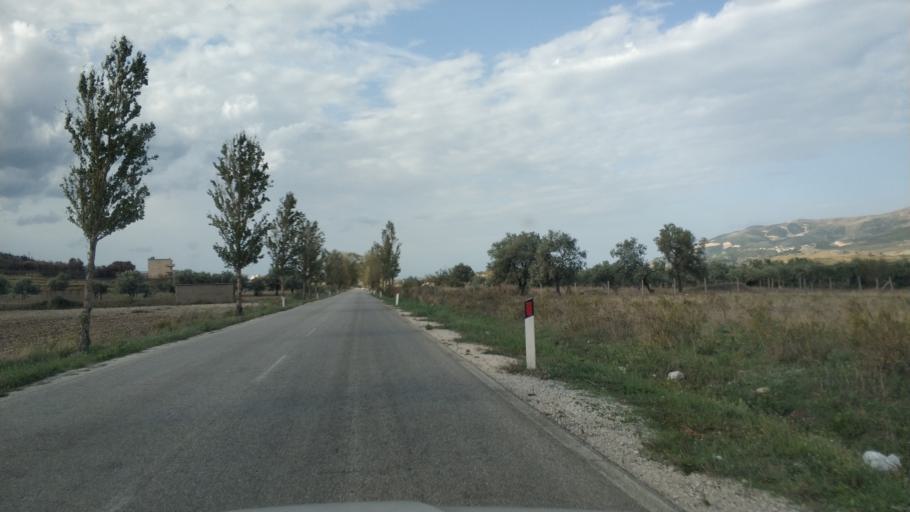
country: AL
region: Vlore
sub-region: Rrethi i Vlores
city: Orikum
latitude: 40.3182
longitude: 19.4835
